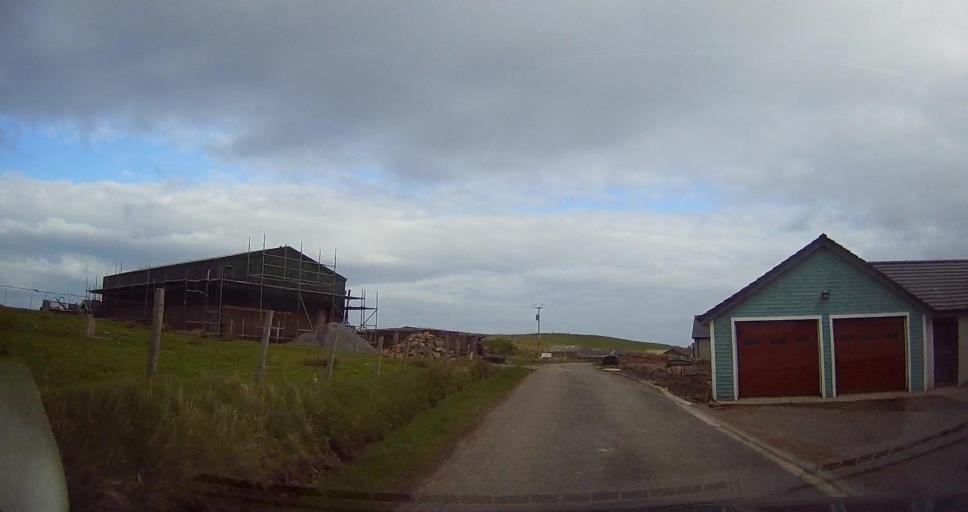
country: GB
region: Scotland
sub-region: Shetland Islands
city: Sandwick
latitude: 60.0435
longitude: -1.2046
